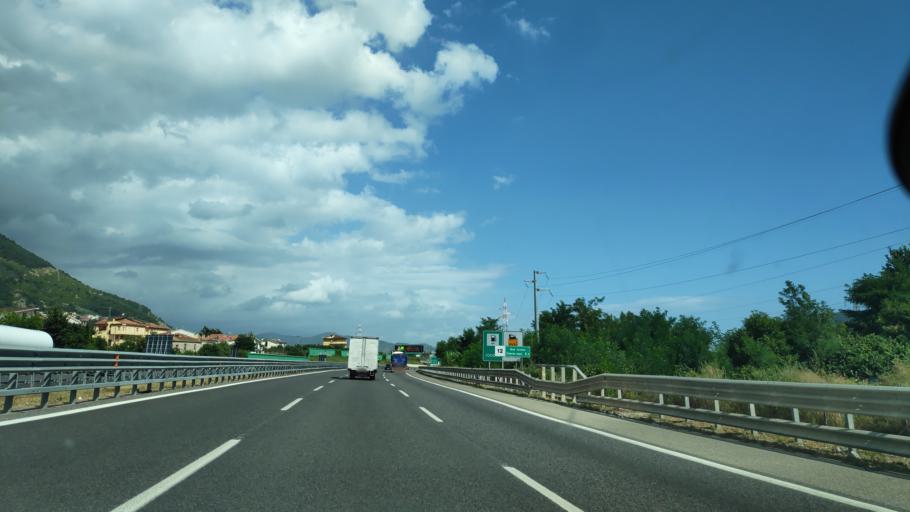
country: IT
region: Campania
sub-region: Provincia di Salerno
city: Piegolelle-San Bartolomeo
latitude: 40.6981
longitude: 14.8234
